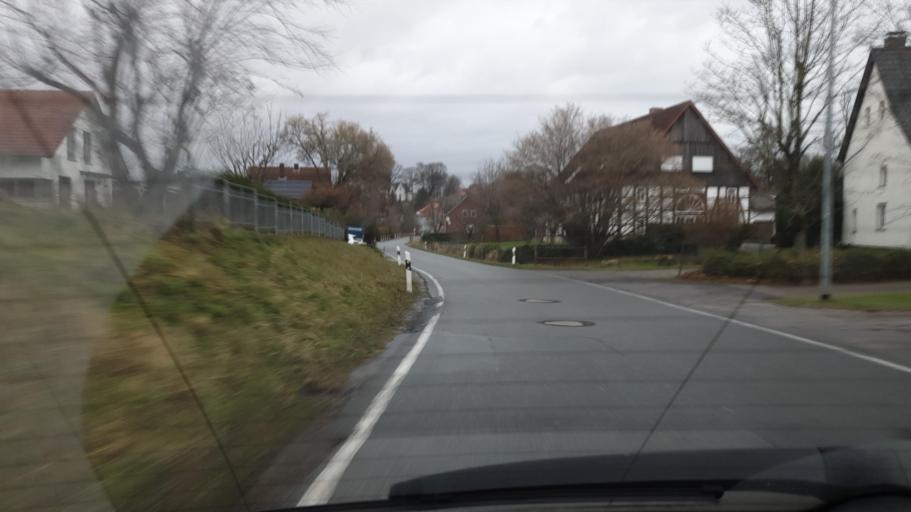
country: DE
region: North Rhine-Westphalia
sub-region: Regierungsbezirk Detmold
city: Detmold
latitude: 51.9756
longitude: 8.8445
